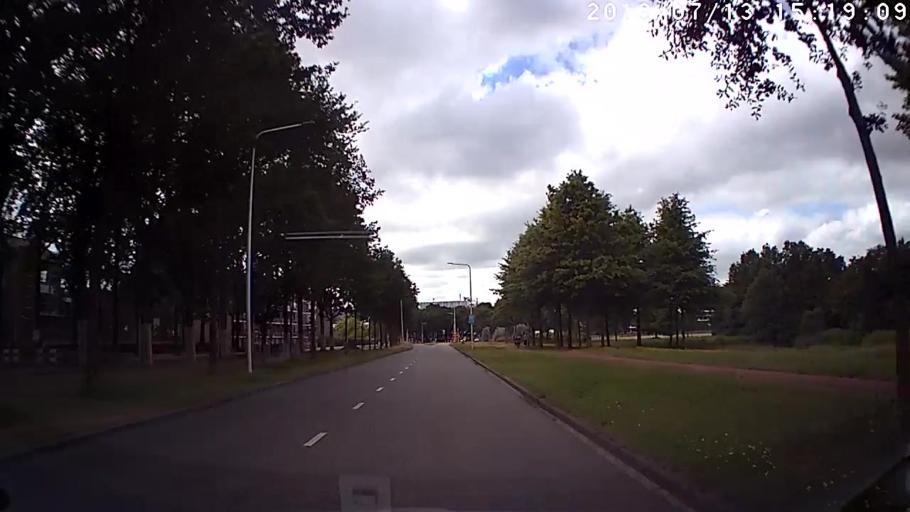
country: NL
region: Overijssel
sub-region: Gemeente Zwolle
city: Zwolle
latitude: 52.5063
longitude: 6.1084
